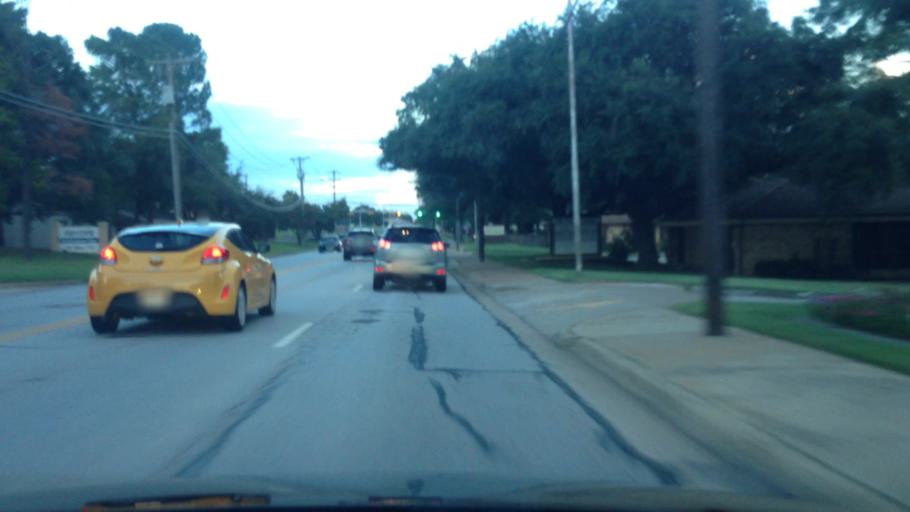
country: US
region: Texas
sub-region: Tarrant County
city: Arlington
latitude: 32.7446
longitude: -97.1318
